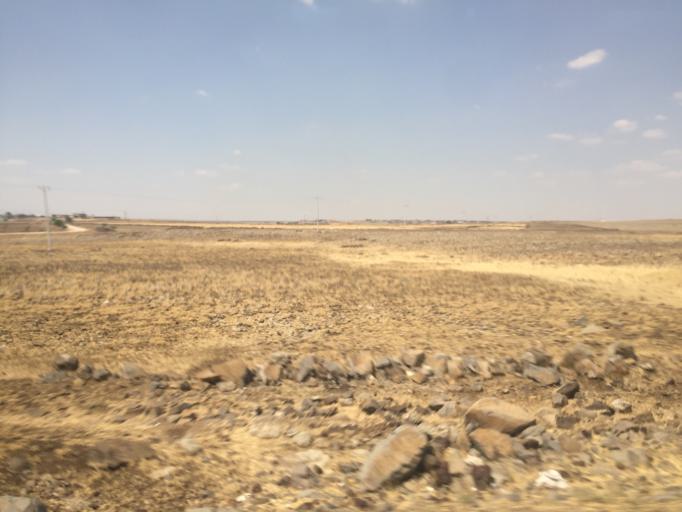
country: TR
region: Sanliurfa
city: Siverek
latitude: 37.7755
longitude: 39.4556
